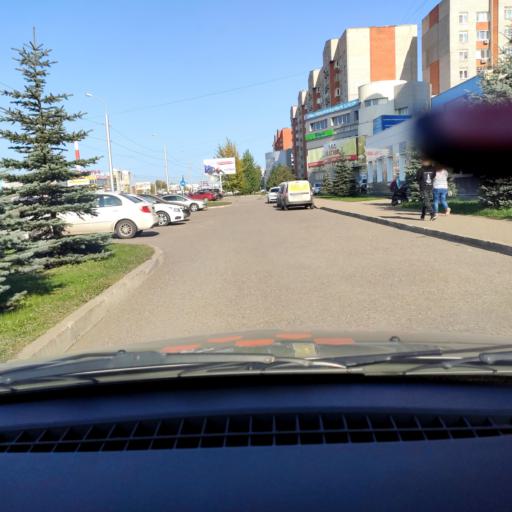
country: RU
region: Bashkortostan
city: Ufa
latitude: 54.7761
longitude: 56.0678
